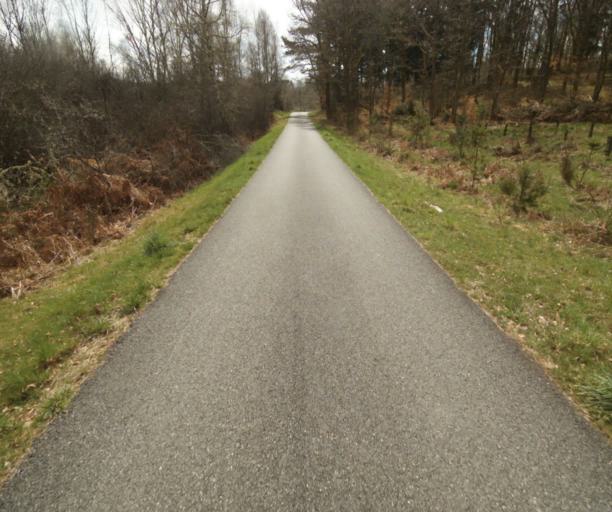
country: FR
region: Limousin
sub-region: Departement de la Correze
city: Egletons
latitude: 45.3706
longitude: 1.9685
